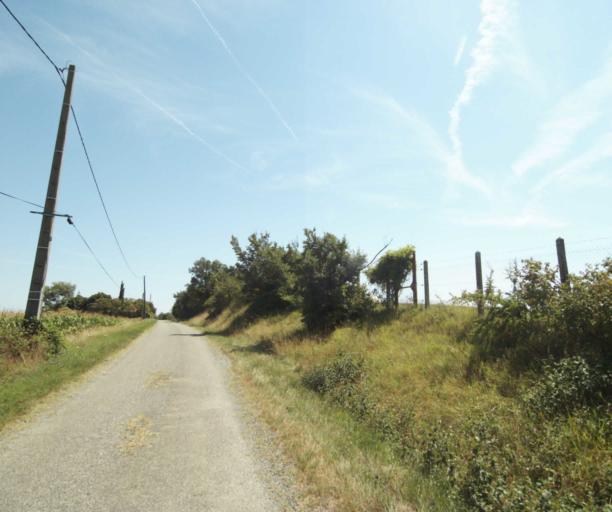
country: FR
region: Midi-Pyrenees
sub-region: Departement de l'Ariege
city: Lezat-sur-Leze
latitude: 43.2542
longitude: 1.3195
